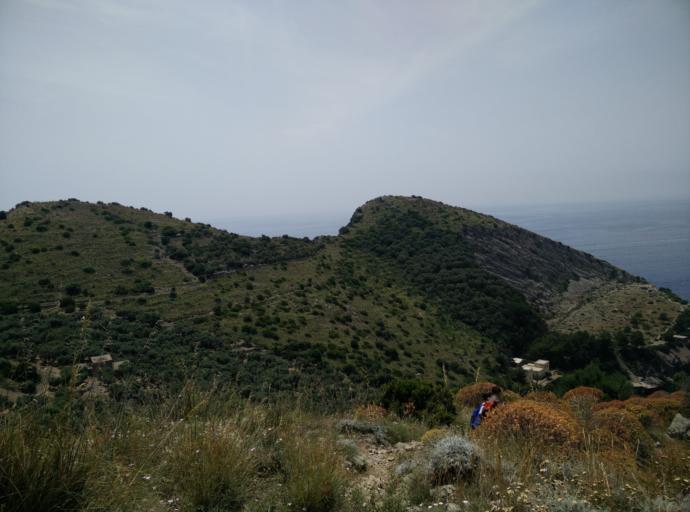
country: IT
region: Campania
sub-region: Provincia di Napoli
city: Massa Lubrense
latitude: 40.5765
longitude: 14.3423
